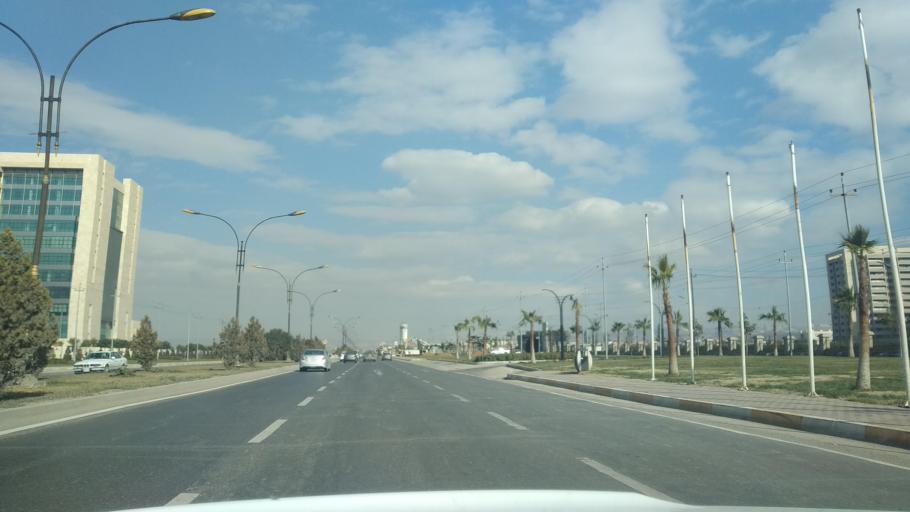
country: IQ
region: Arbil
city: Erbil
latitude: 36.2460
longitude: 44.0709
